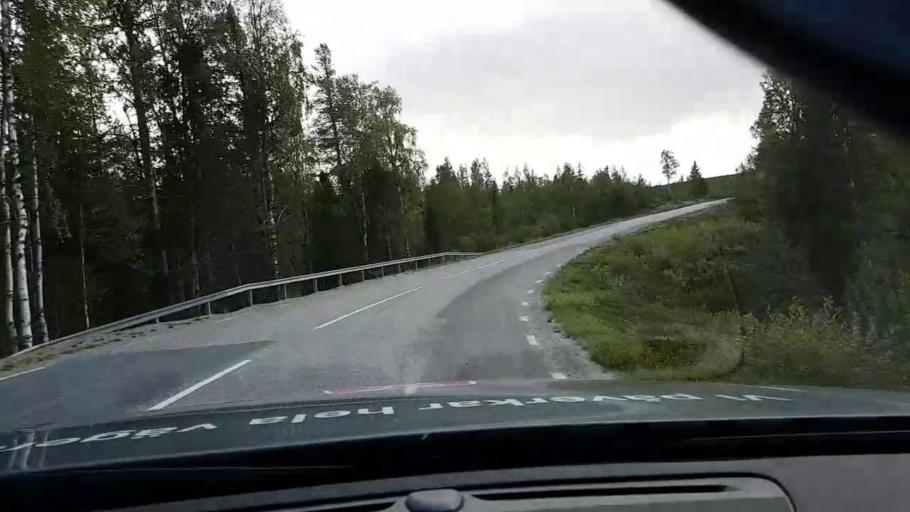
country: SE
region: Vaesterbotten
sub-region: Asele Kommun
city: Asele
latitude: 63.8055
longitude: 17.5472
